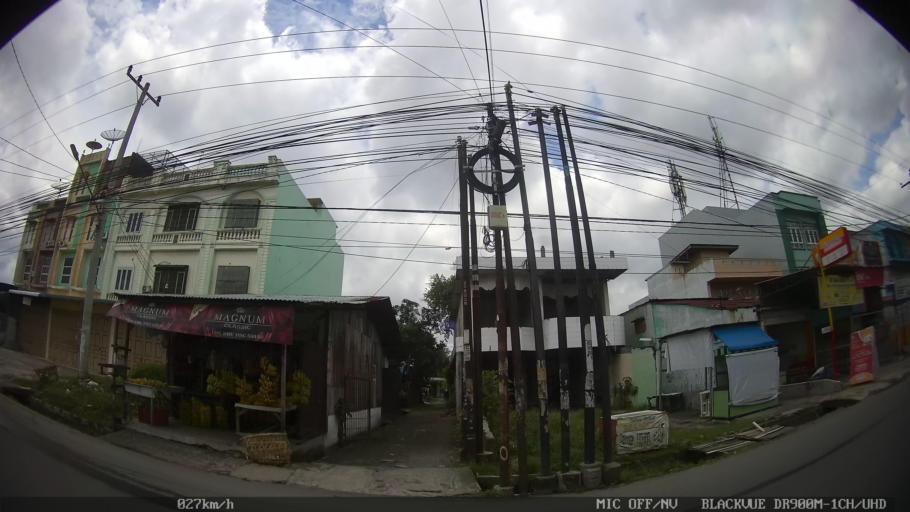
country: ID
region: North Sumatra
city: Medan
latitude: 3.6207
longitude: 98.7076
